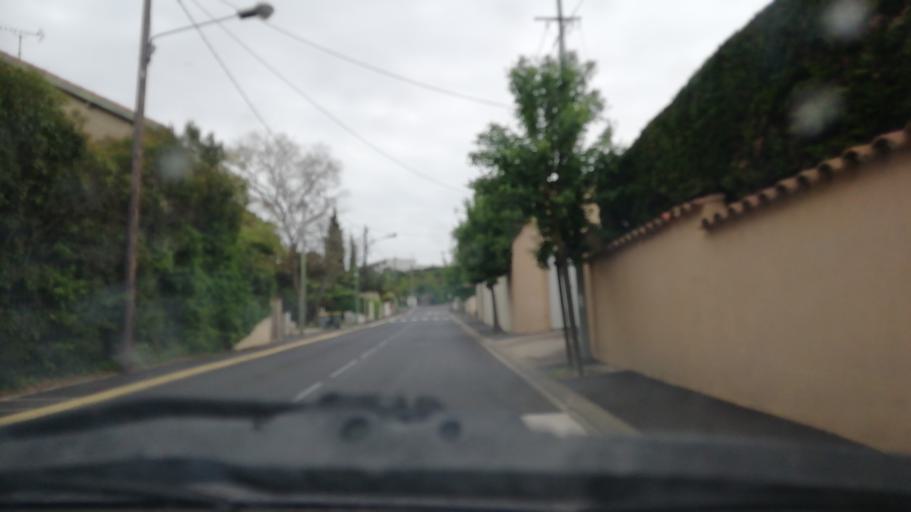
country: FR
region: Languedoc-Roussillon
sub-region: Departement de l'Herault
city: Boujan-sur-Libron
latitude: 43.3696
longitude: 3.2522
